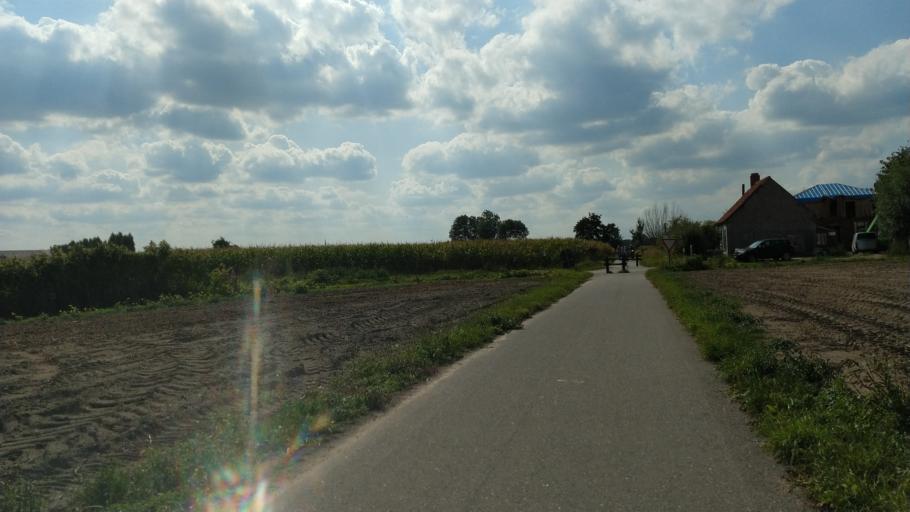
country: BE
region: Flanders
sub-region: Provincie Oost-Vlaanderen
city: Assenede
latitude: 51.2431
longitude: 3.6930
